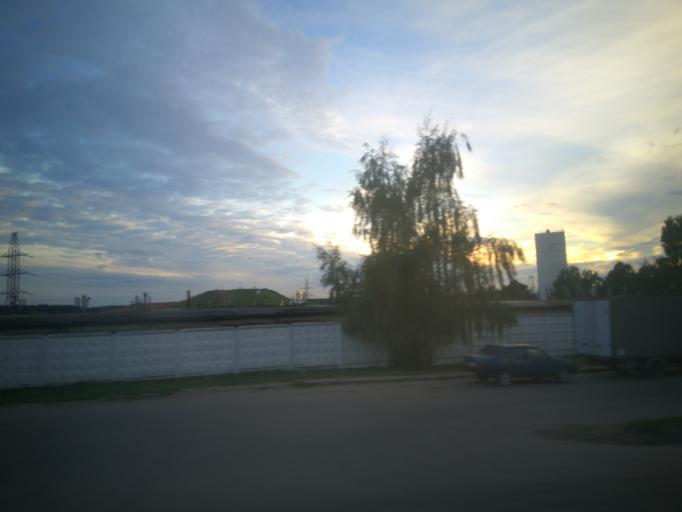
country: RU
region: Moscow
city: Solntsevo
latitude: 55.6341
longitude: 37.3877
